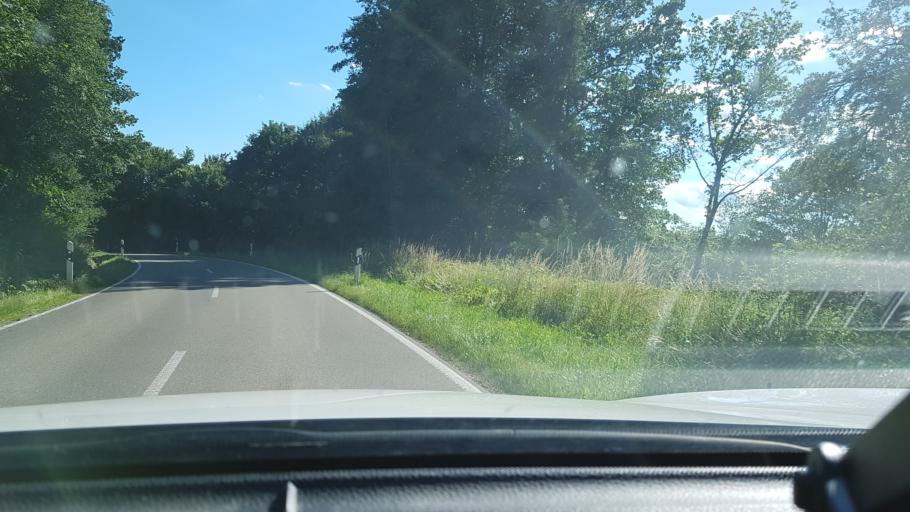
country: DE
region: Baden-Wuerttemberg
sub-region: Tuebingen Region
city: Gutenzell-Hurbel
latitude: 48.1436
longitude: 10.0010
